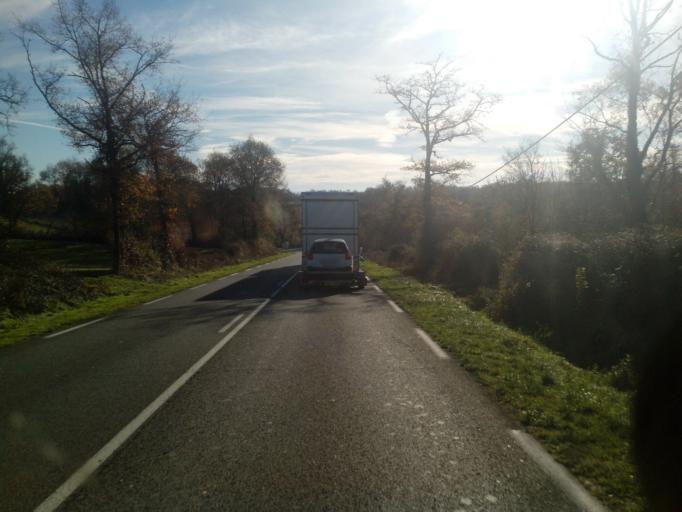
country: FR
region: Limousin
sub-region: Departement de la Haute-Vienne
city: Bellac
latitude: 46.1021
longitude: 1.0752
